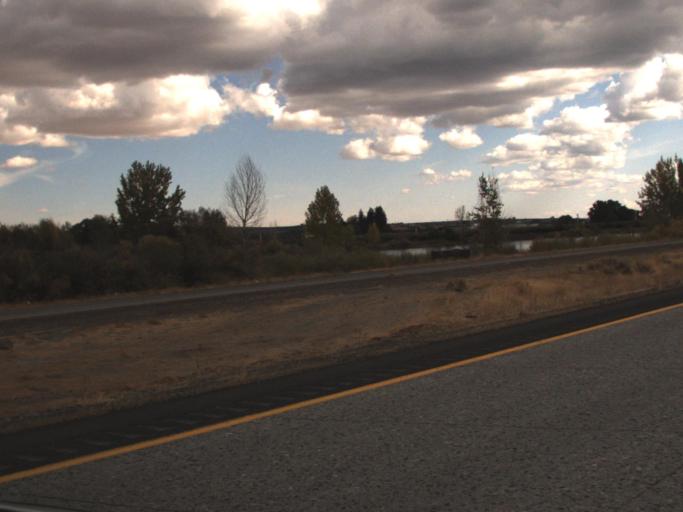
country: US
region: Washington
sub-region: Yakima County
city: Wapato
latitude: 46.4808
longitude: -120.4078
